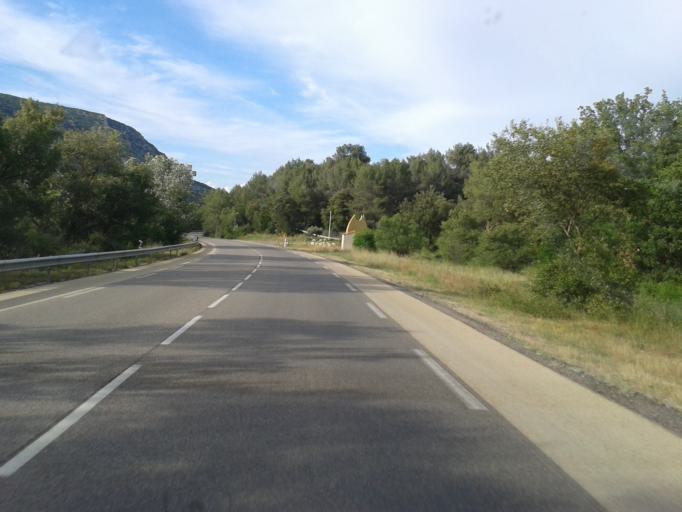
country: FR
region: Provence-Alpes-Cote d'Azur
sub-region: Departement des Bouches-du-Rhone
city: Jouques
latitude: 43.6684
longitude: 5.6478
